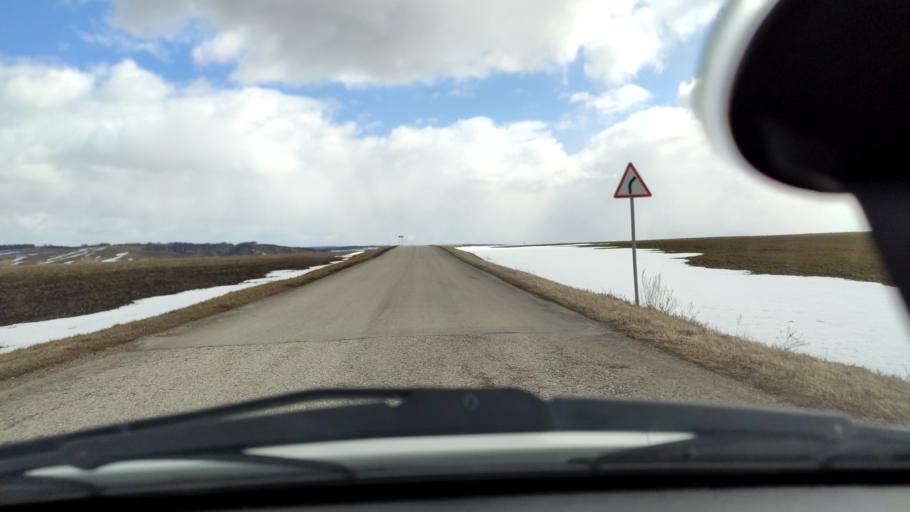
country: RU
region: Bashkortostan
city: Tolbazy
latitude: 54.1710
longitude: 55.9226
